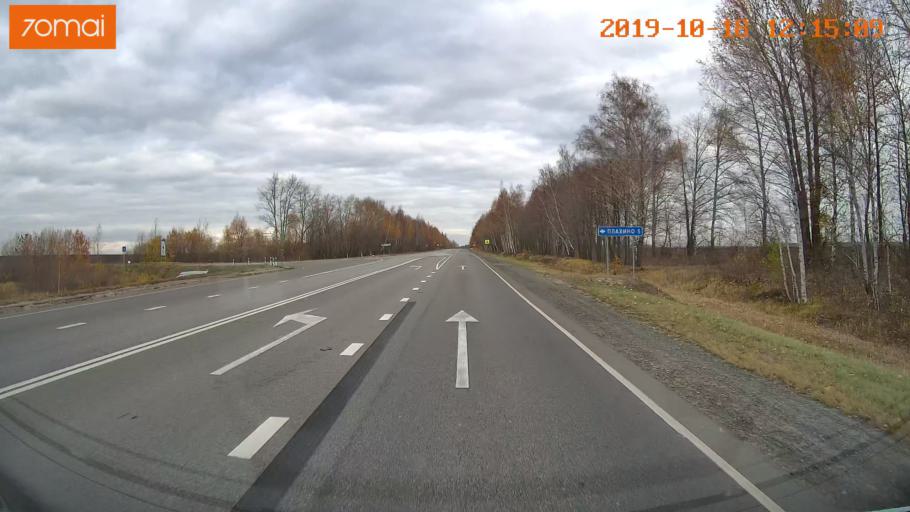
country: RU
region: Rjazan
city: Zakharovo
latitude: 54.4397
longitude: 39.3951
